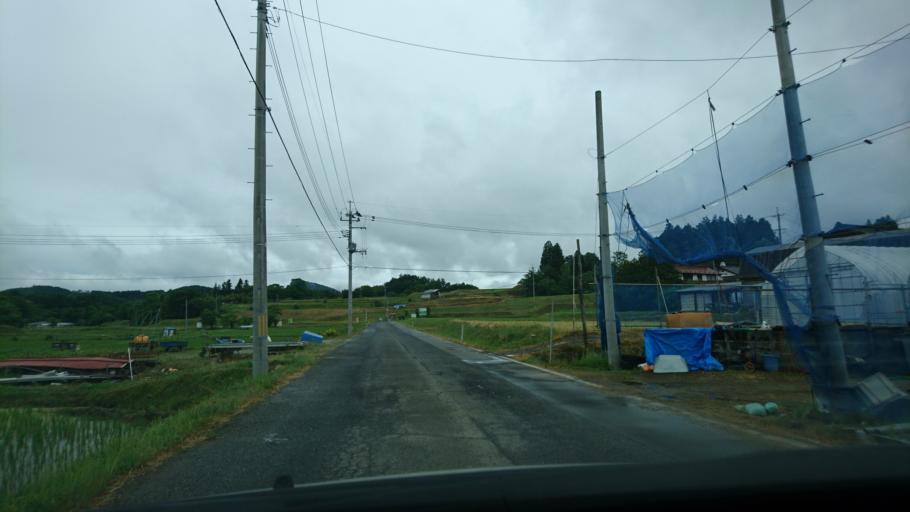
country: JP
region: Iwate
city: Ichinoseki
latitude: 38.9241
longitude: 141.2093
